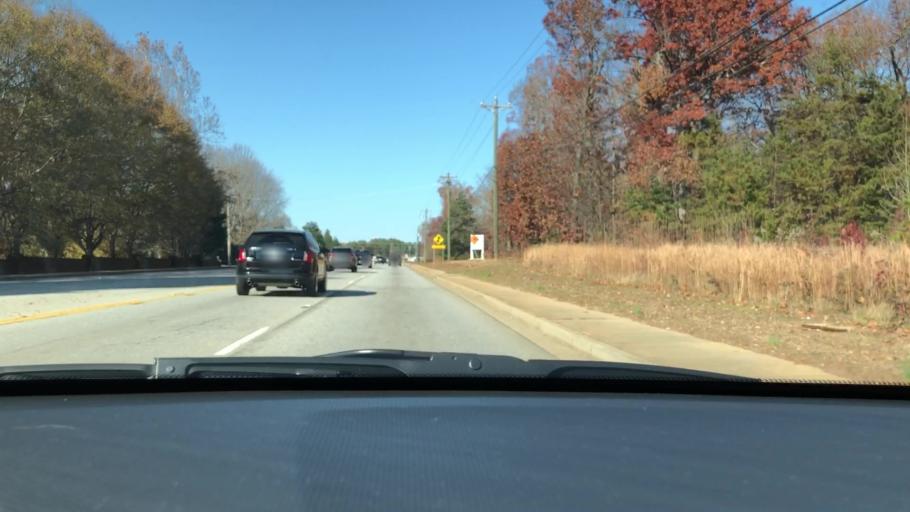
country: US
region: South Carolina
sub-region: Greenville County
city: Five Forks
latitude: 34.8107
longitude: -82.2399
